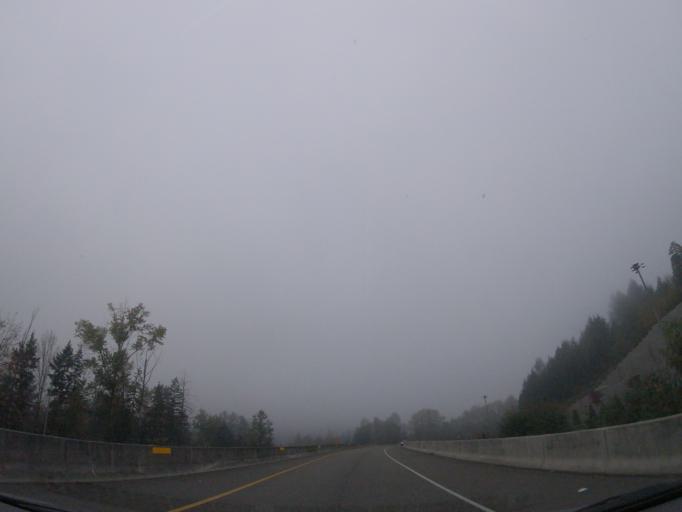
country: US
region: Washington
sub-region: King County
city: Bothell
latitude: 47.7559
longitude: -122.1920
